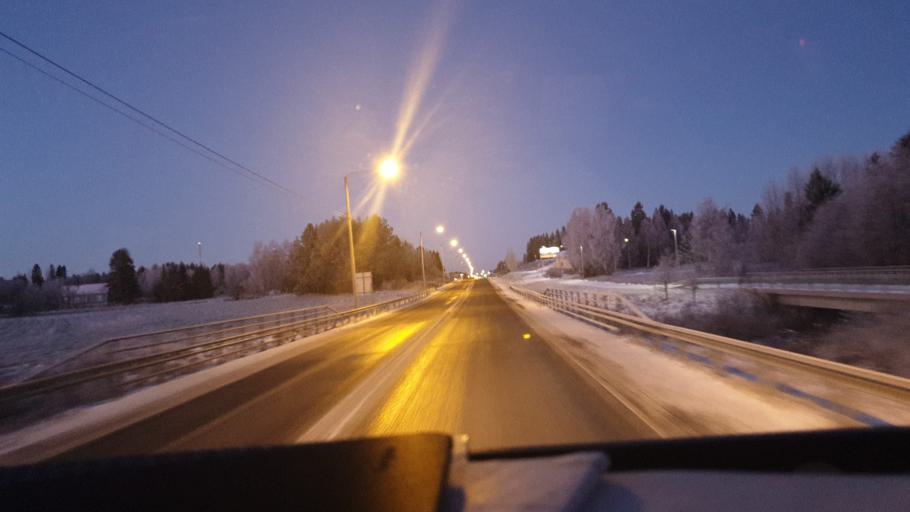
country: FI
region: Northern Ostrobothnia
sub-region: Raahe
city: Raahe
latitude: 64.6872
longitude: 24.5834
